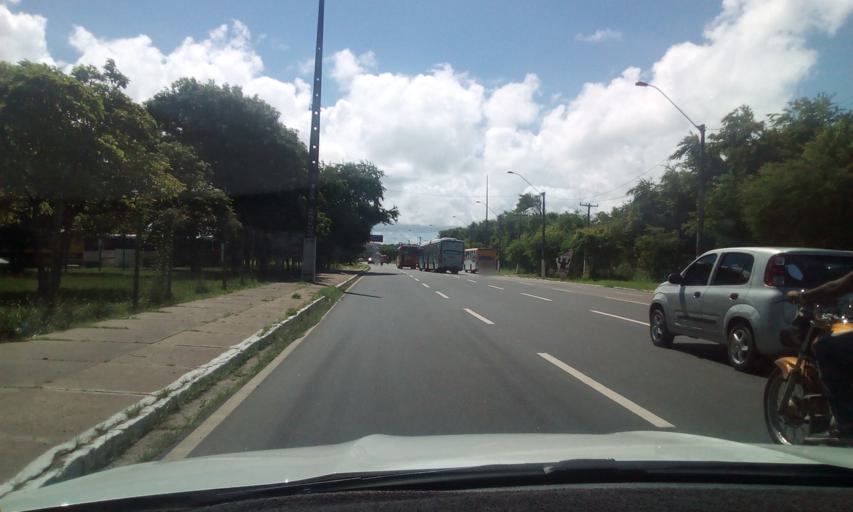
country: BR
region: Pernambuco
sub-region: Recife
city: Recife
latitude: -8.0327
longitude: -34.8665
